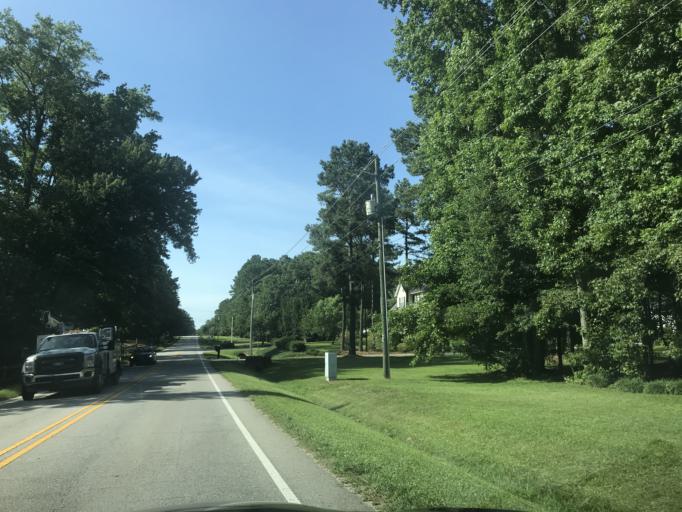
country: US
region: North Carolina
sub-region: Johnston County
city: Clayton
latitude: 35.6434
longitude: -78.5387
